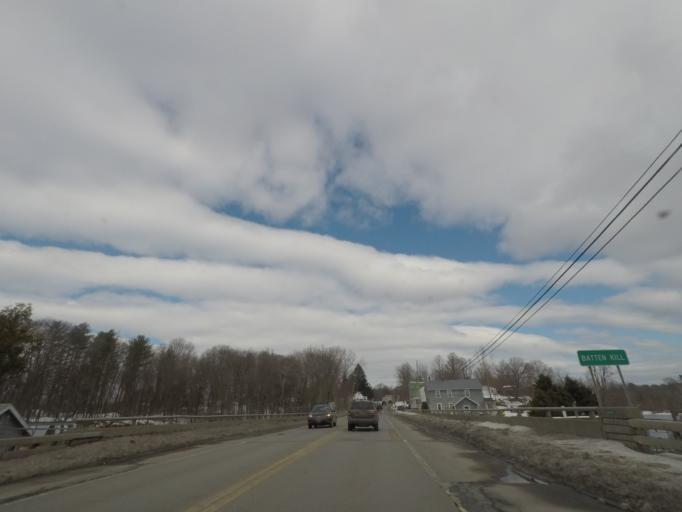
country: US
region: New York
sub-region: Washington County
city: Greenwich
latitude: 43.0986
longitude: -73.5251
